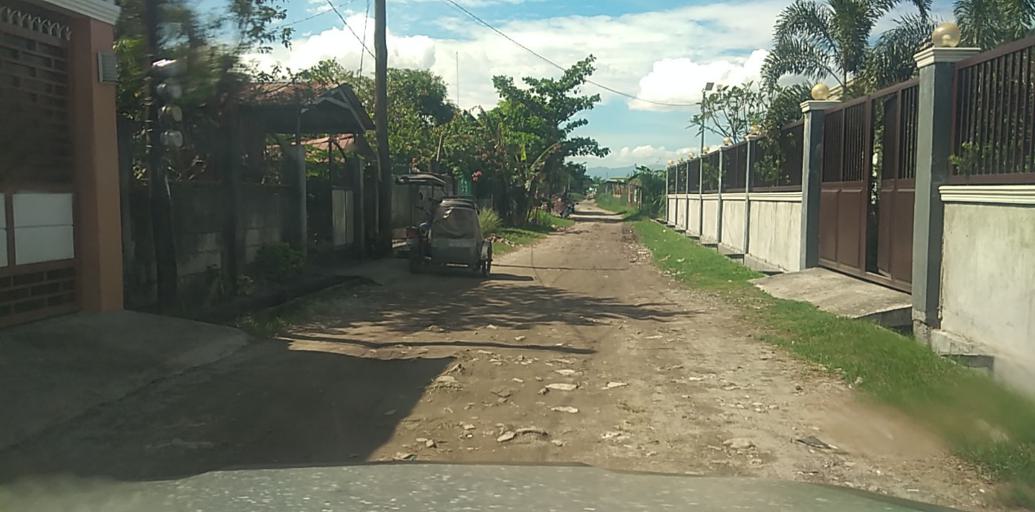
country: PH
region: Central Luzon
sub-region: Province of Pampanga
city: Buensuseso
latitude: 15.1946
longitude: 120.6712
